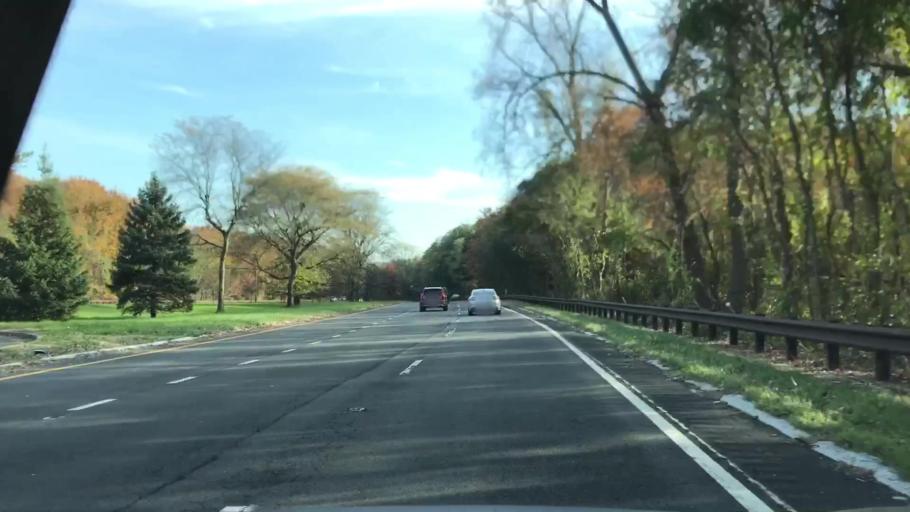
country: US
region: New York
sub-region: Rockland County
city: Tappan
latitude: 41.0264
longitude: -73.9381
